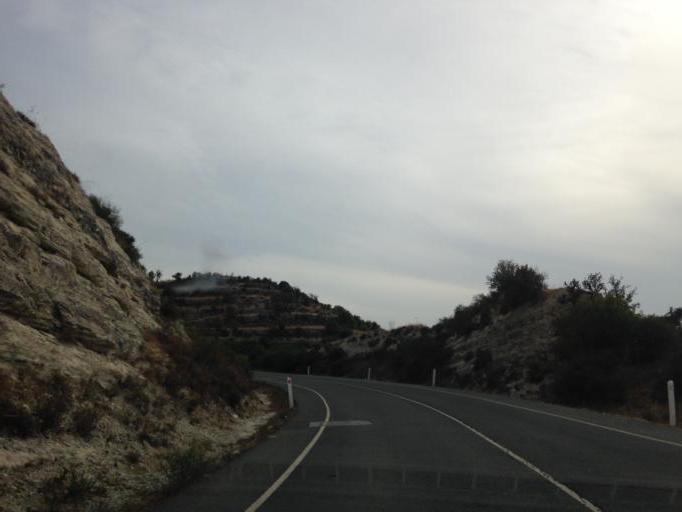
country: CY
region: Limassol
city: Pachna
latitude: 34.8047
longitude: 32.7902
